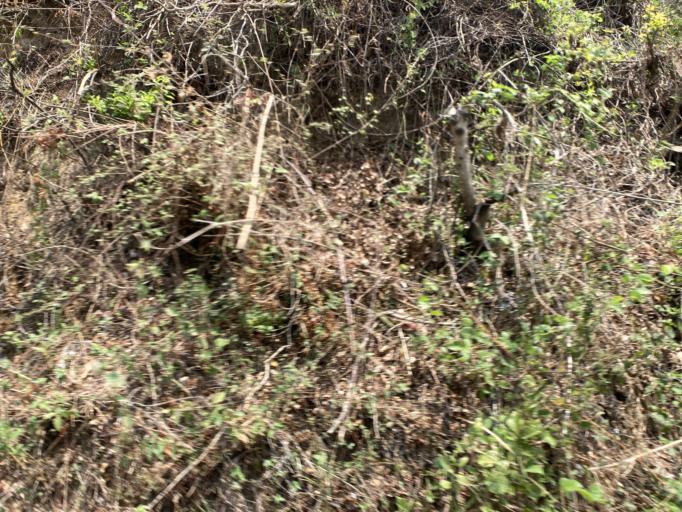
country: GT
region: Escuintla
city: San Vicente Pacaya
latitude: 14.3809
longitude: -90.5524
